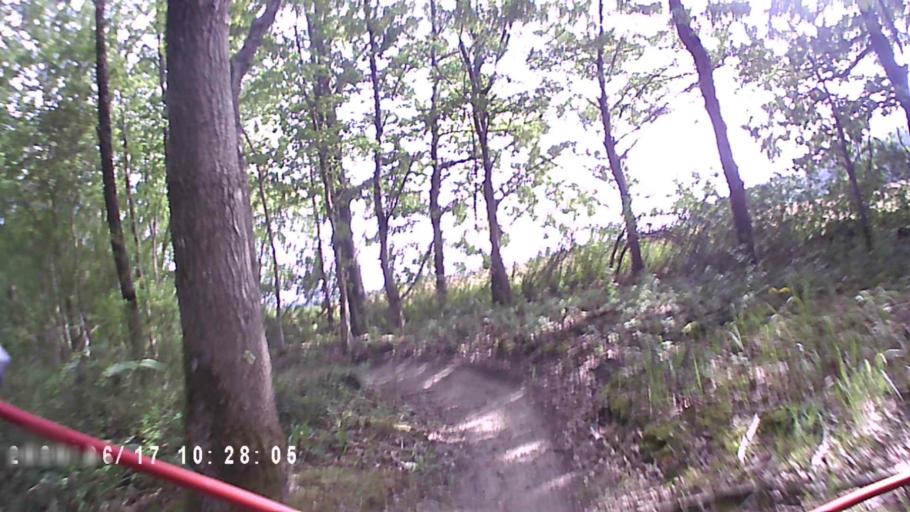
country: NL
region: Groningen
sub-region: Gemeente De Marne
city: Ulrum
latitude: 53.3951
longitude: 6.2416
